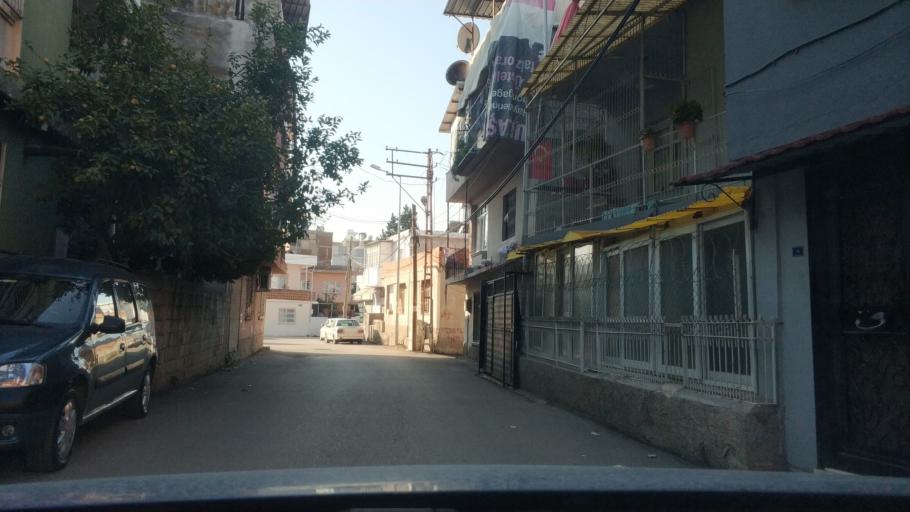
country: TR
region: Adana
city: Adana
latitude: 37.0093
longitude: 35.3122
